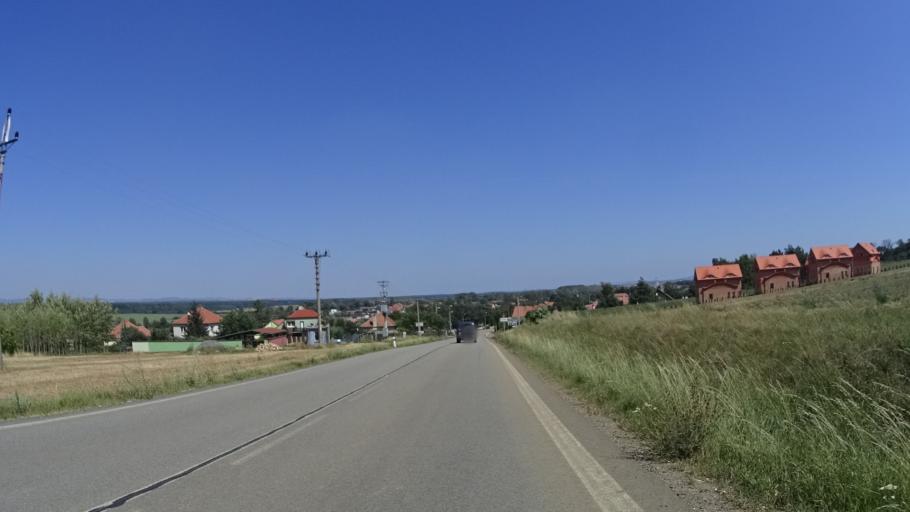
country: CZ
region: South Moravian
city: Petrov
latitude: 48.8769
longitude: 17.2669
